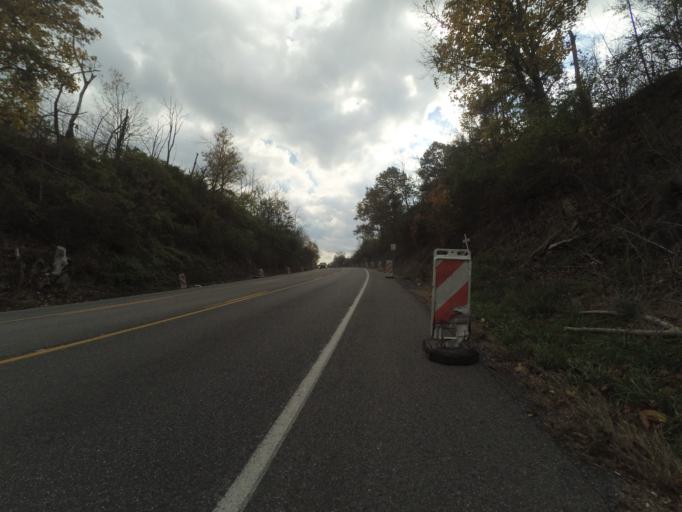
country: US
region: Pennsylvania
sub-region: Centre County
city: Bellefonte
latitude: 40.8998
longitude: -77.7901
